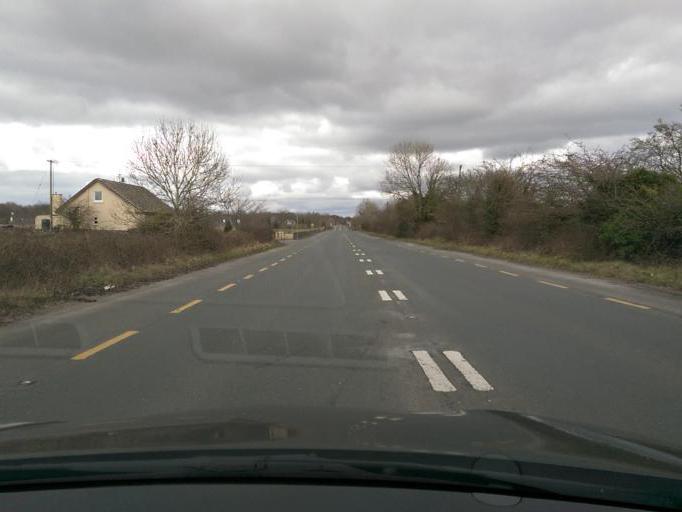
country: IE
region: Connaught
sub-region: County Galway
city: Ballinasloe
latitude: 53.3532
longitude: -8.0803
